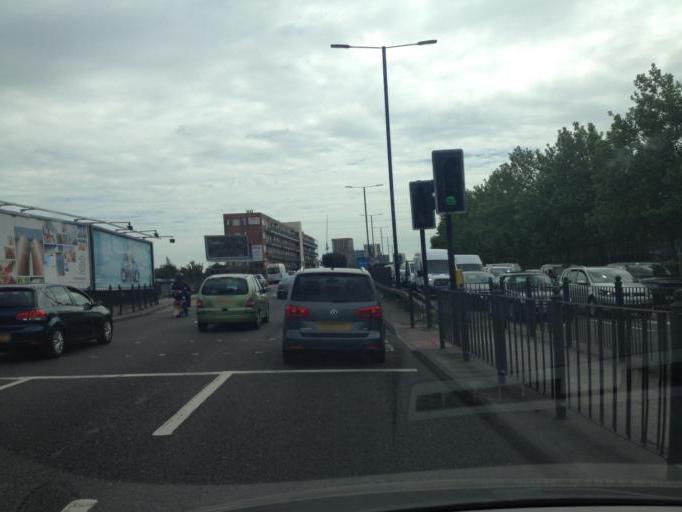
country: GB
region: England
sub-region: Greater London
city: Acton
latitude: 51.5262
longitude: -0.2740
